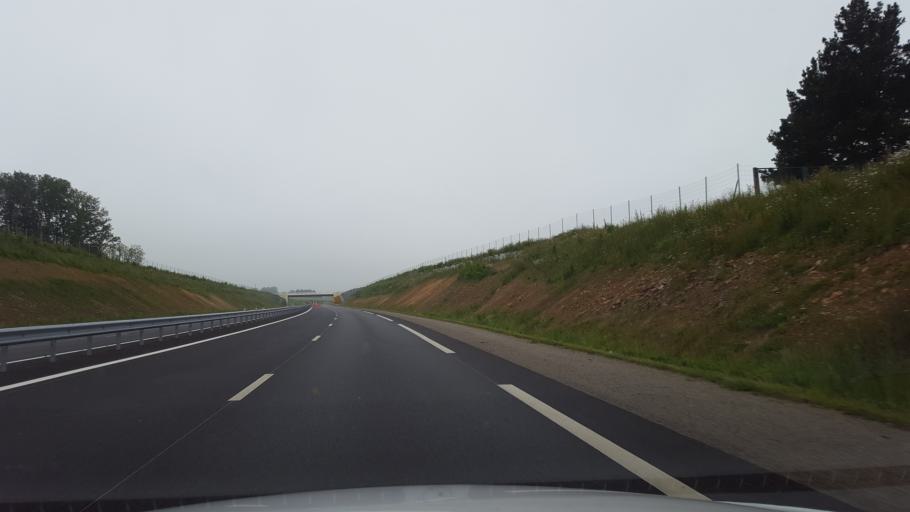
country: FR
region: Brittany
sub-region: Departement d'Ille-et-Vilaine
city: Guignen
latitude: 47.9144
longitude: -1.8597
